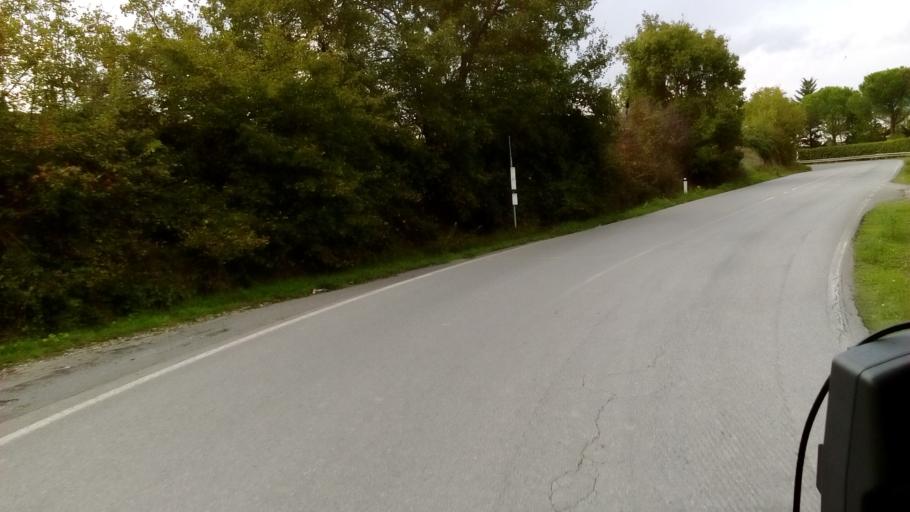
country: IT
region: Tuscany
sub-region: Province of Florence
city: Montespertoli
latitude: 43.6526
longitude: 11.0861
